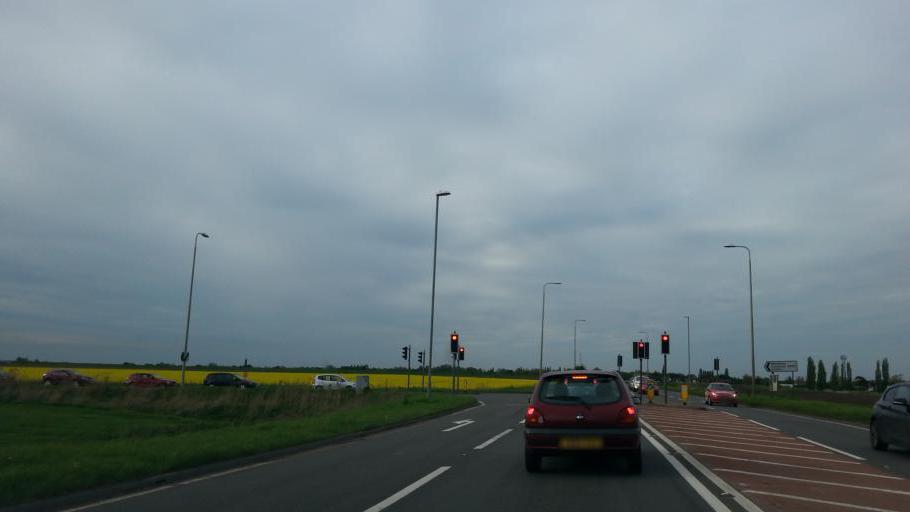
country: GB
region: England
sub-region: Cambridgeshire
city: March
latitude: 52.5925
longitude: 0.0598
